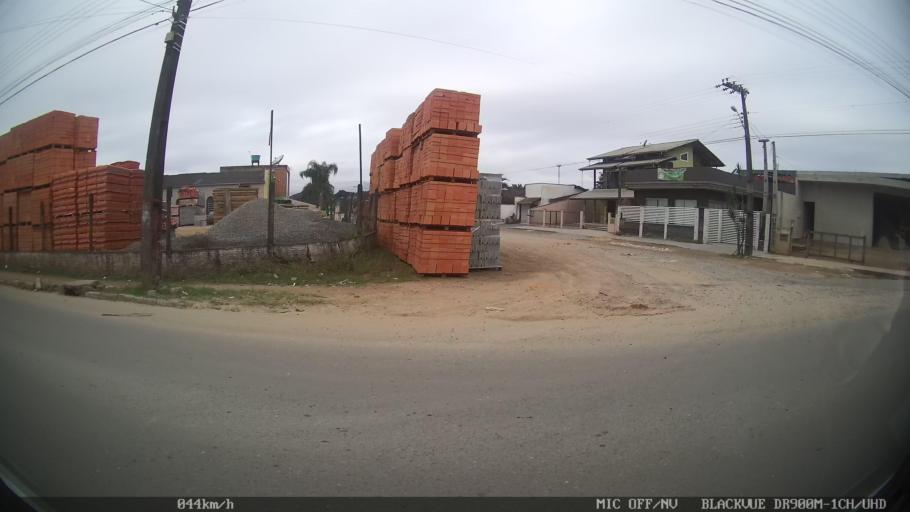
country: BR
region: Santa Catarina
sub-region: Joinville
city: Joinville
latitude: -26.3313
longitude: -48.9063
